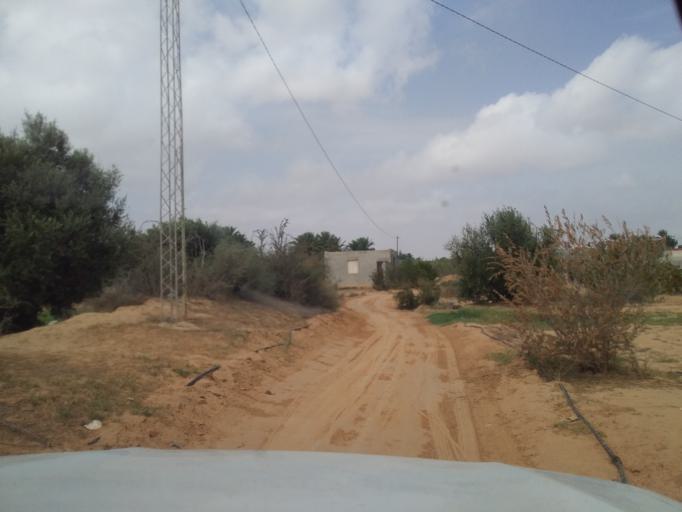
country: TN
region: Qabis
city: Gabes
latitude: 33.6265
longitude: 10.2959
